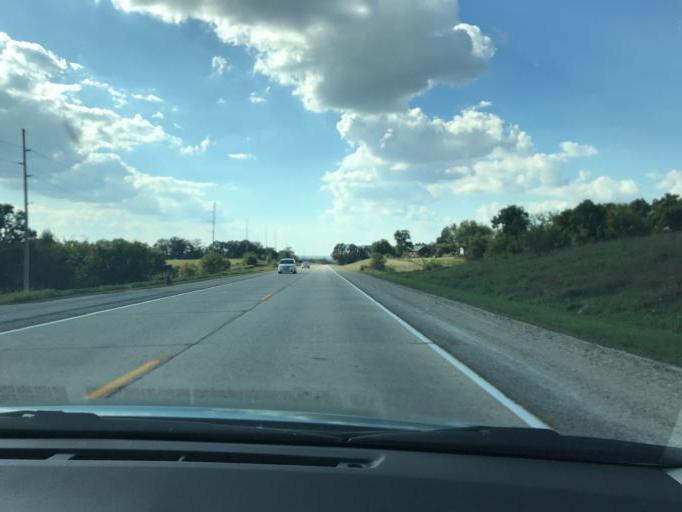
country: US
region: Wisconsin
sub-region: Green County
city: Brodhead
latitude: 42.5591
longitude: -89.3116
